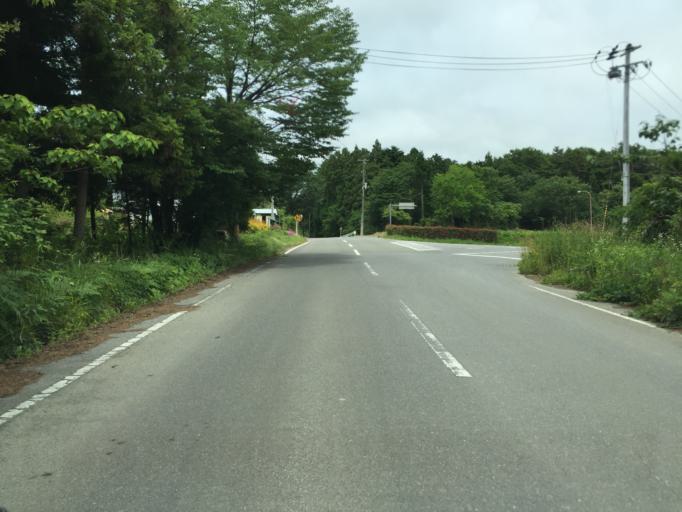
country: JP
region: Fukushima
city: Namie
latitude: 37.7224
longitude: 140.9802
